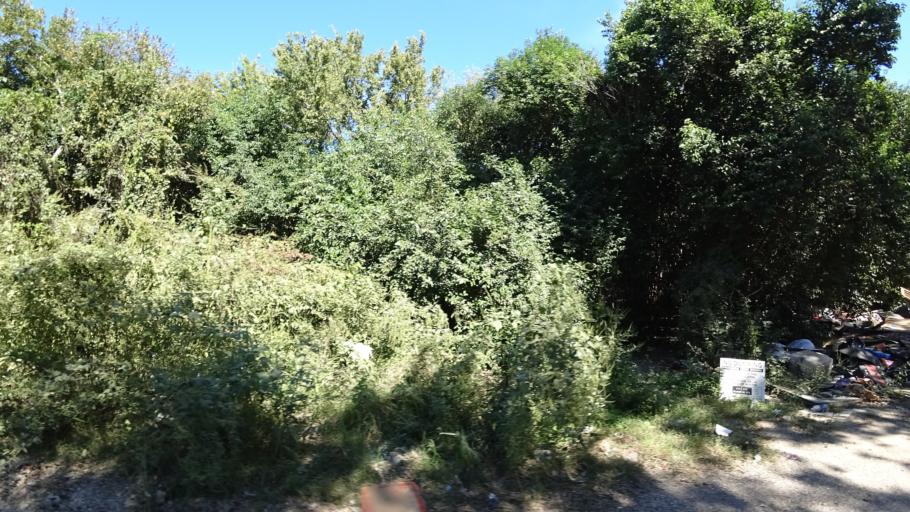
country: US
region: Texas
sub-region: Travis County
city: Austin
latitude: 30.2114
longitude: -97.6871
